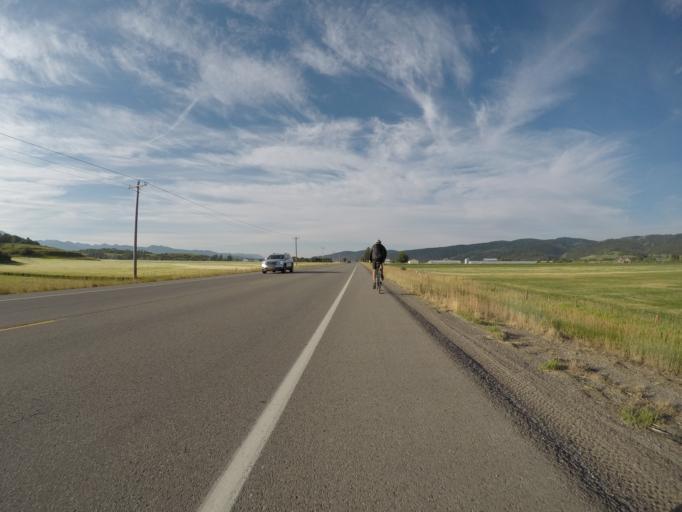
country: US
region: Wyoming
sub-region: Lincoln County
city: Afton
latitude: 42.9345
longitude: -111.0074
